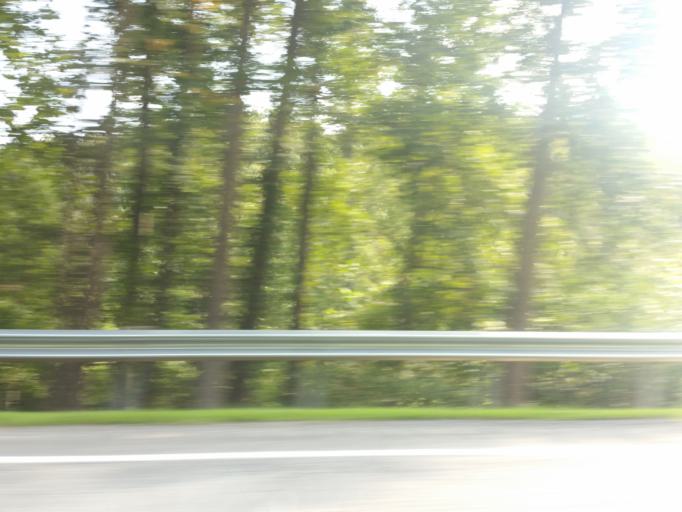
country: US
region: Kentucky
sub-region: Bell County
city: Pineville
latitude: 36.7300
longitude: -83.6563
